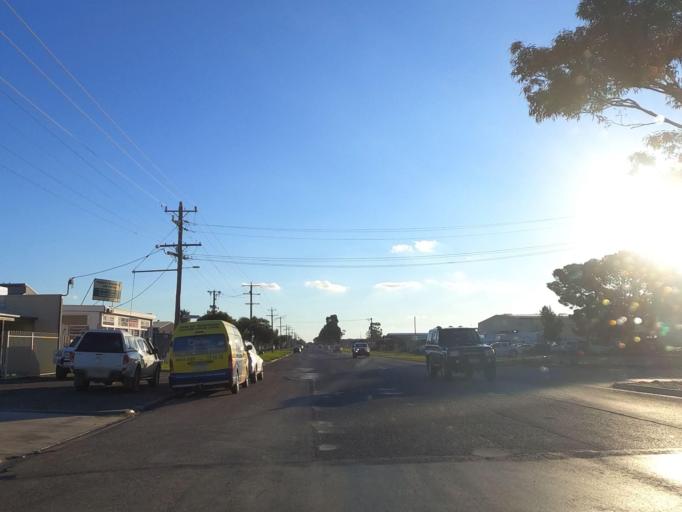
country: AU
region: Victoria
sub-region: Swan Hill
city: Swan Hill
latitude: -35.3268
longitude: 143.5485
